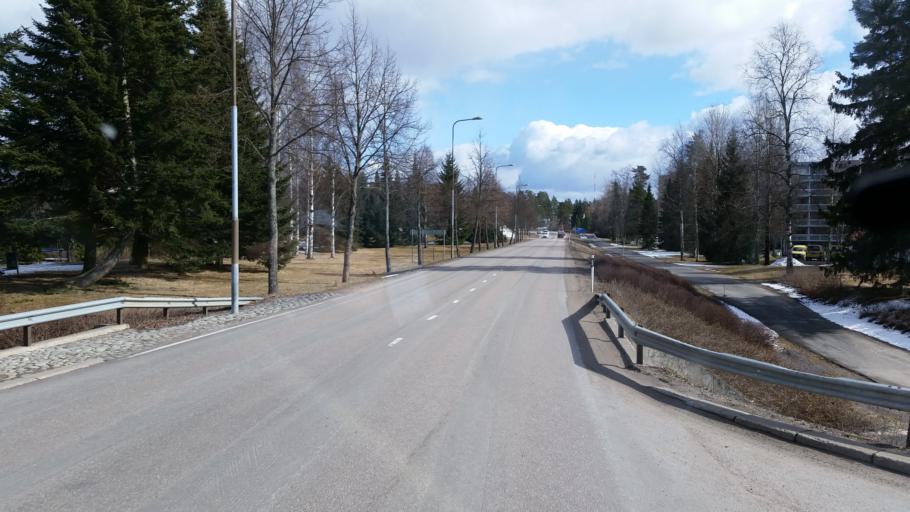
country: FI
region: South Karelia
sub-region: Imatra
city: Imatra
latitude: 61.1706
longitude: 28.7589
